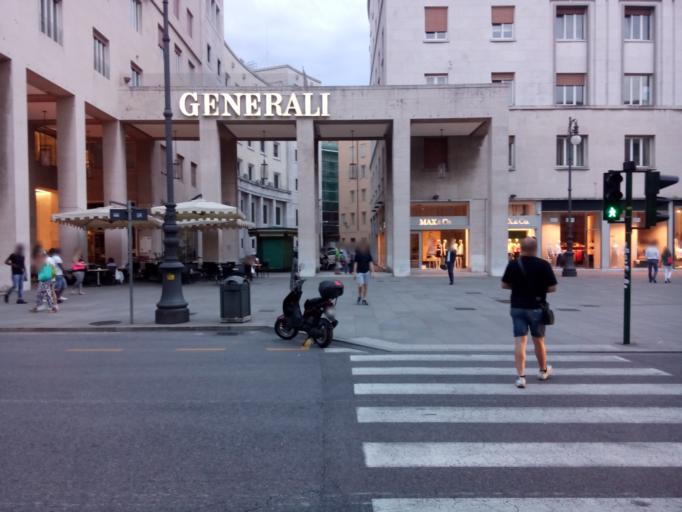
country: IT
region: Friuli Venezia Giulia
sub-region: Provincia di Trieste
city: Trieste
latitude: 45.6503
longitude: 13.7712
